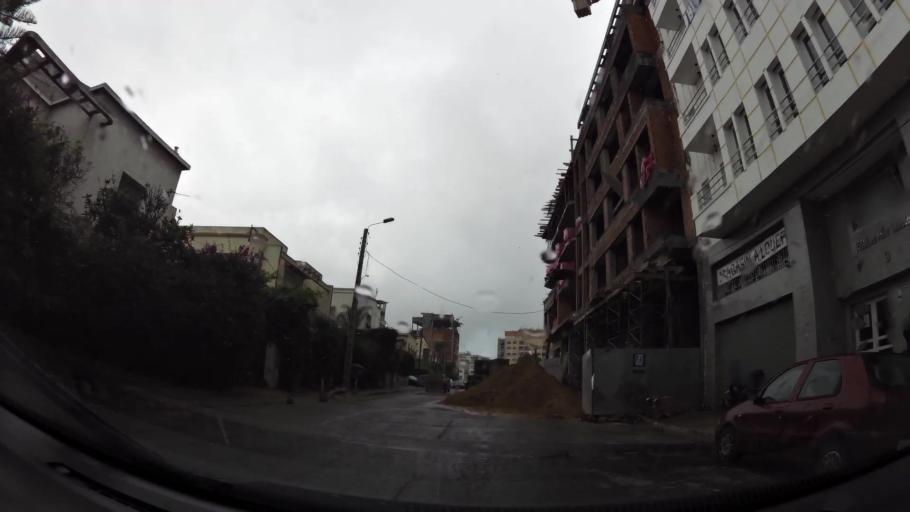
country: MA
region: Grand Casablanca
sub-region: Casablanca
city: Casablanca
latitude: 33.5700
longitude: -7.6181
